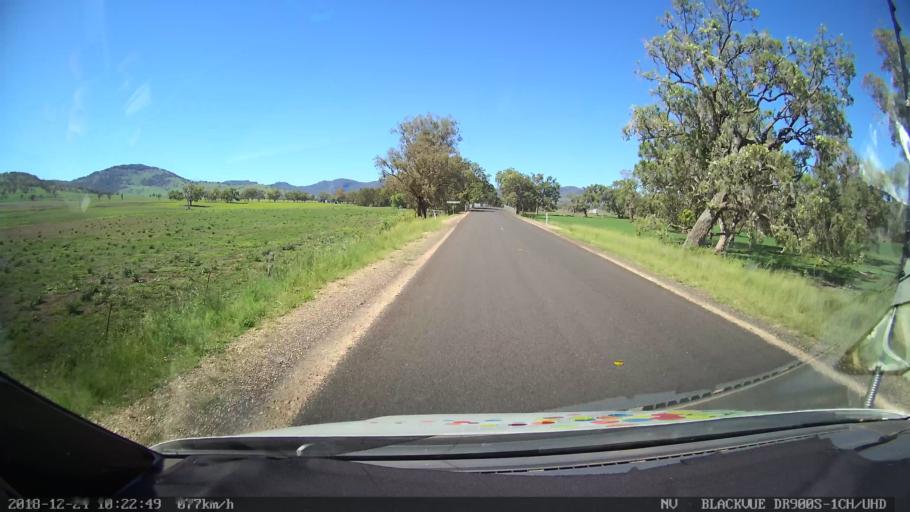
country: AU
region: New South Wales
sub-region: Liverpool Plains
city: Quirindi
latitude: -31.7686
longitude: 150.5421
